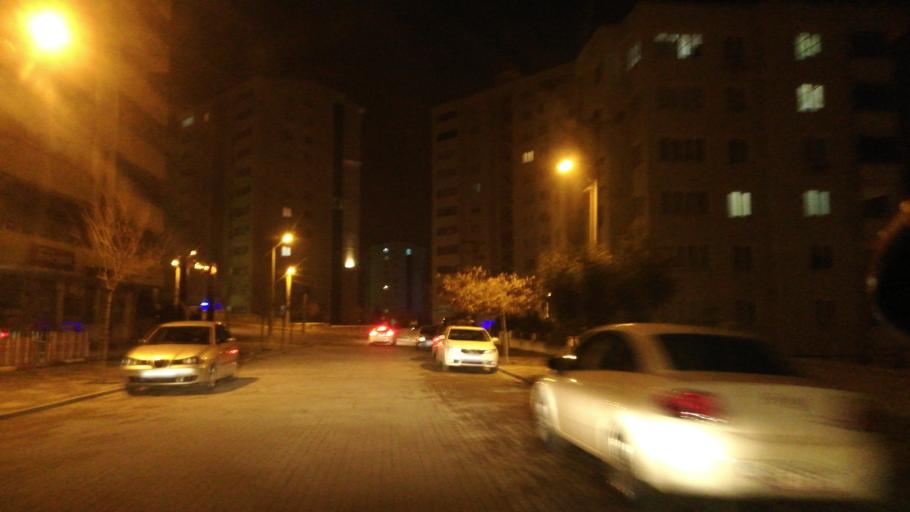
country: TR
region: Kahramanmaras
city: Kahramanmaras
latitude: 37.5971
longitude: 36.8869
